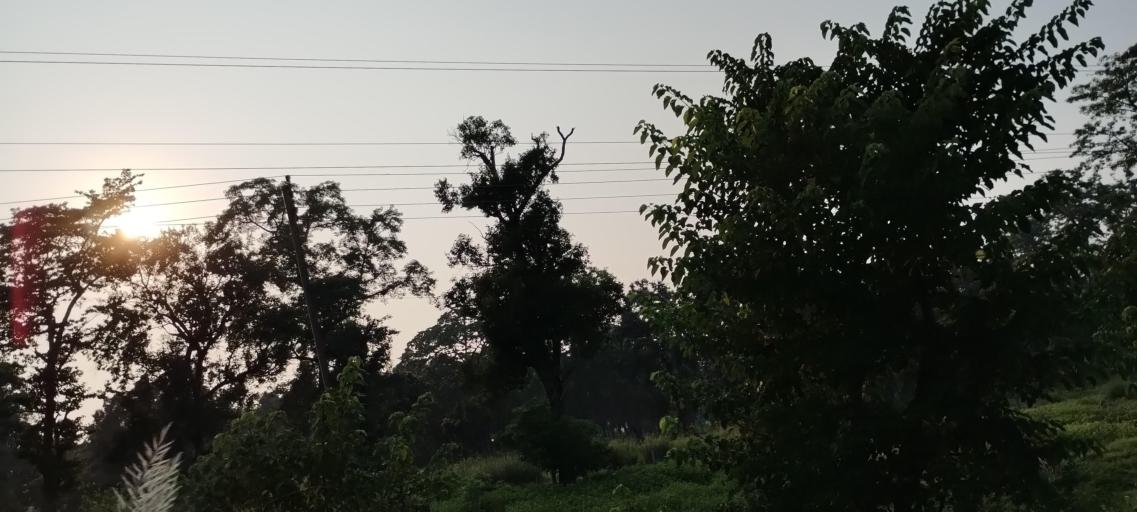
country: NP
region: Far Western
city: Tikapur
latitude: 28.5079
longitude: 81.3247
